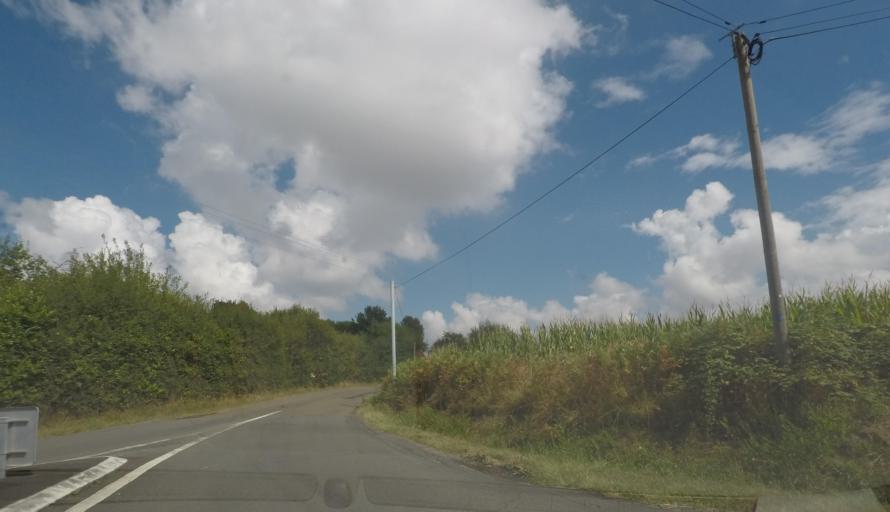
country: FR
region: Pays de la Loire
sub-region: Departement de la Sarthe
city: Saint-Cosme-en-Vairais
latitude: 48.2606
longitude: 0.5345
